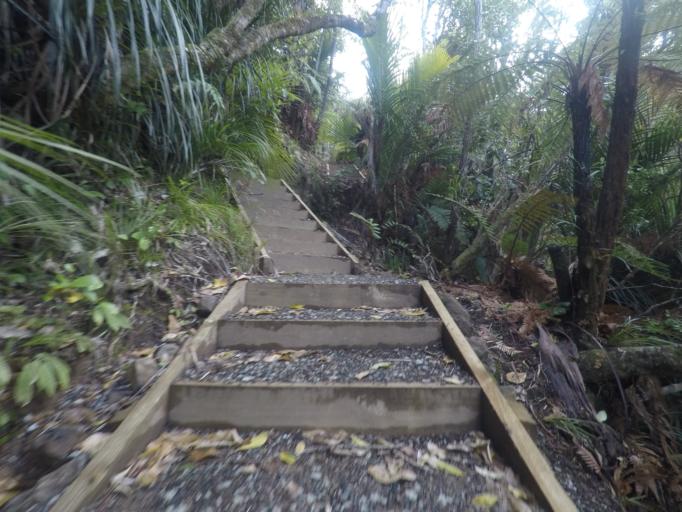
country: NZ
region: Auckland
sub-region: Auckland
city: Titirangi
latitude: -37.0000
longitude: 174.5472
